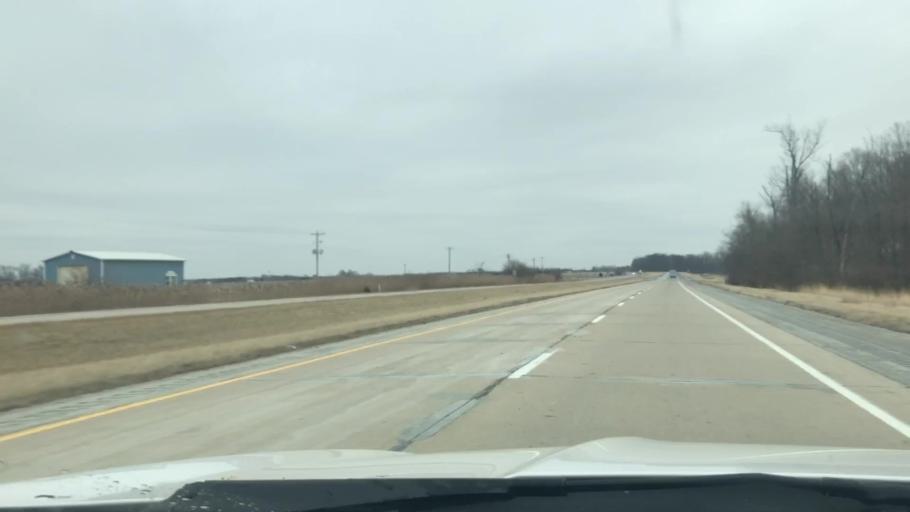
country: US
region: Indiana
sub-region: Cass County
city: Logansport
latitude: 40.7366
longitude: -86.2837
